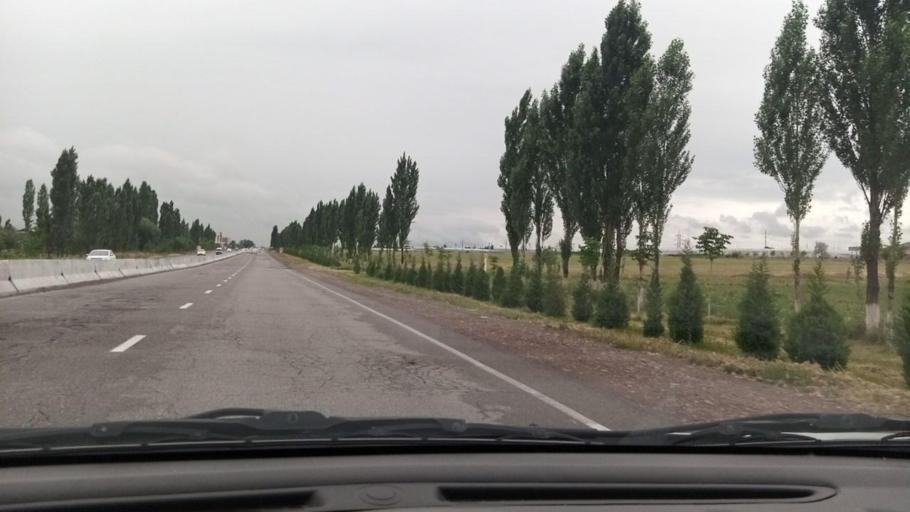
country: UZ
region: Toshkent
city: Ohangaron
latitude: 40.9132
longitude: 69.8206
